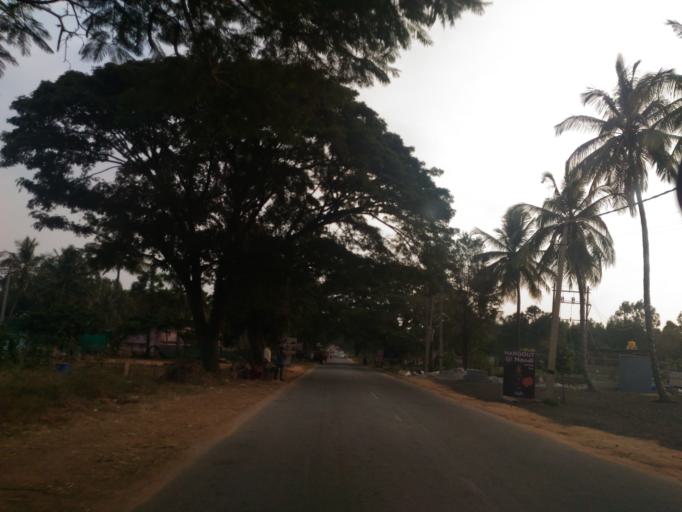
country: IN
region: Karnataka
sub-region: Chikkaballapur
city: Chik Ballapur
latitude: 13.3462
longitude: 77.6870
